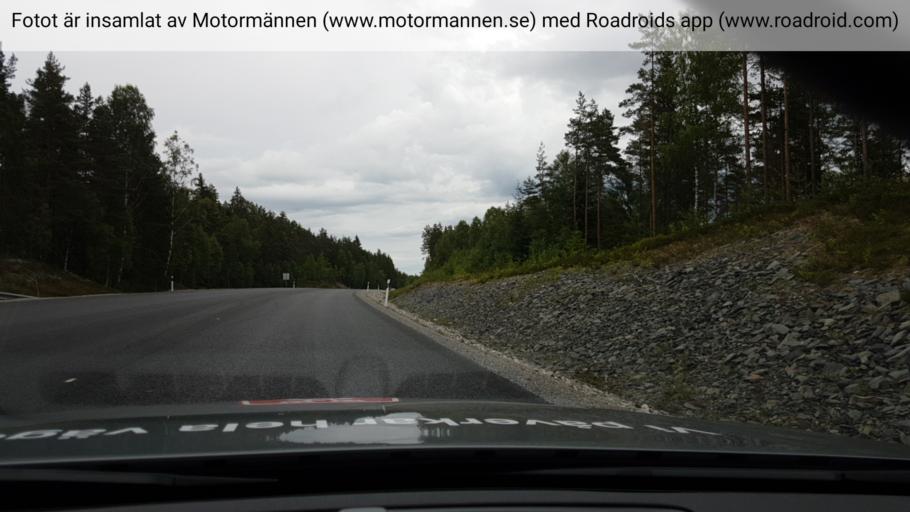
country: SE
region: Vaestmanland
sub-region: Skinnskattebergs Kommun
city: Skinnskatteberg
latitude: 59.8302
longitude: 15.5399
